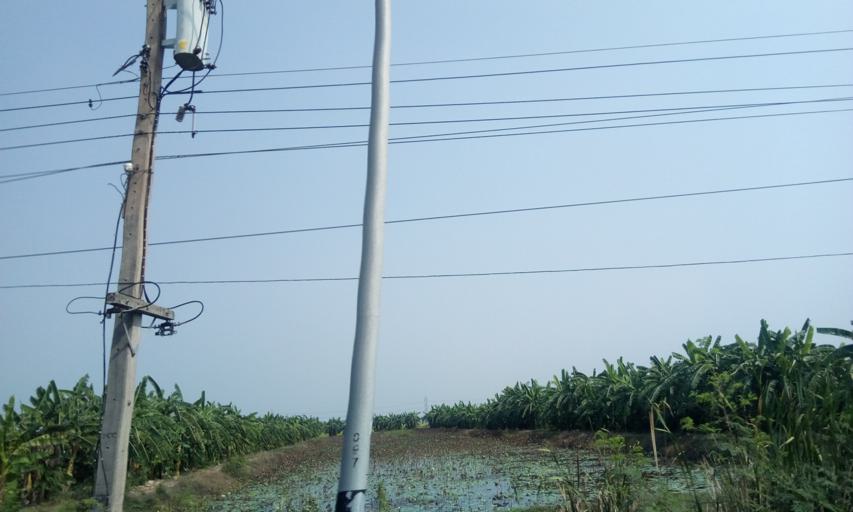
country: TH
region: Pathum Thani
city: Ban Lam Luk Ka
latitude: 13.9894
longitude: 100.7562
